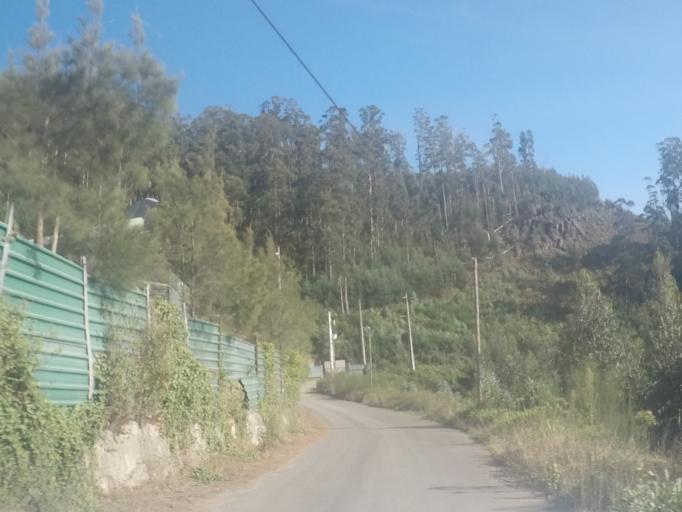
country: PT
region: Madeira
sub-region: Funchal
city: Nossa Senhora do Monte
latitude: 32.6929
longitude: -16.9082
